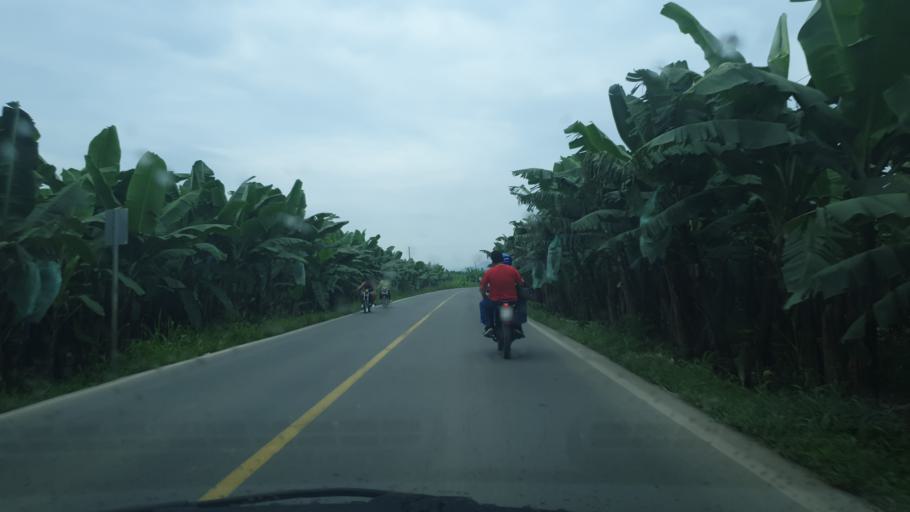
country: EC
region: El Oro
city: Pasaje
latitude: -3.3602
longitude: -79.8346
